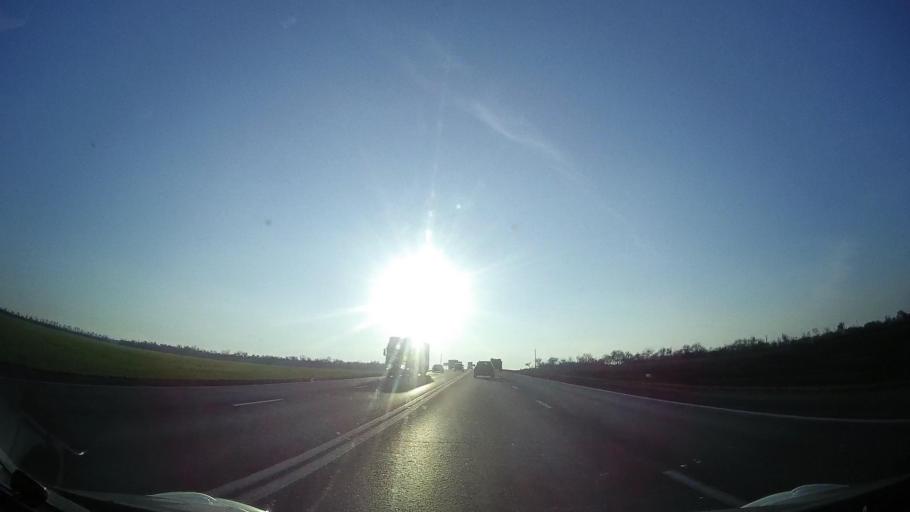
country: RU
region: Rostov
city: Bataysk
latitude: 47.0916
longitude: 39.7973
